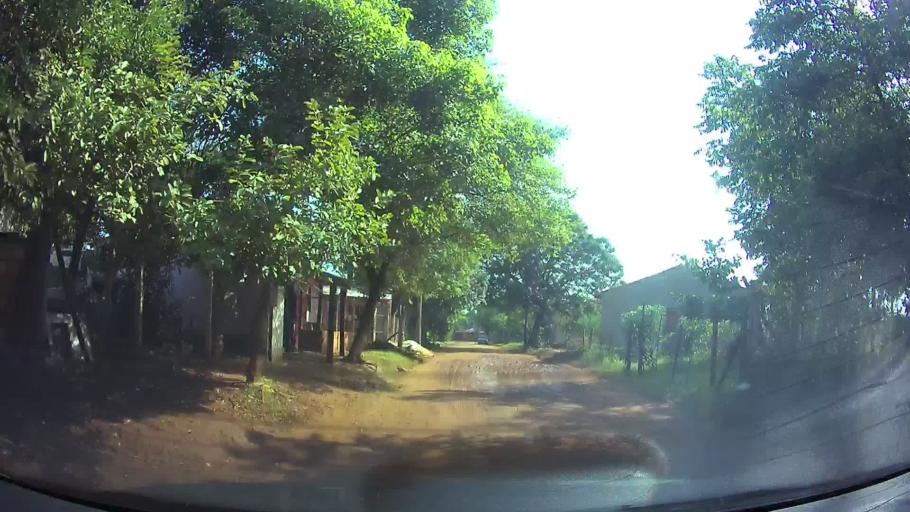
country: PY
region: Central
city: Limpio
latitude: -25.2414
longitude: -57.4661
